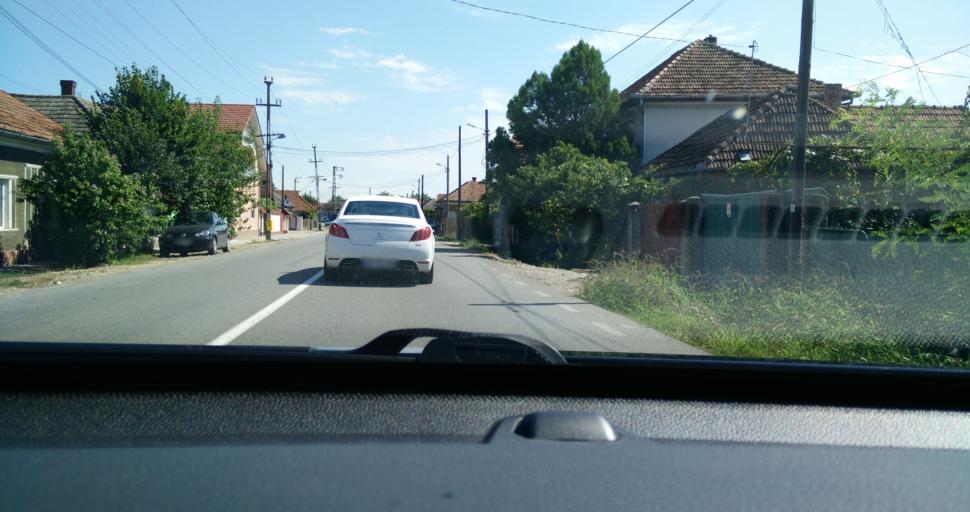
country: RO
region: Bihor
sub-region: Comuna Osorheiu
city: Alparea
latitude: 47.0413
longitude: 22.0300
